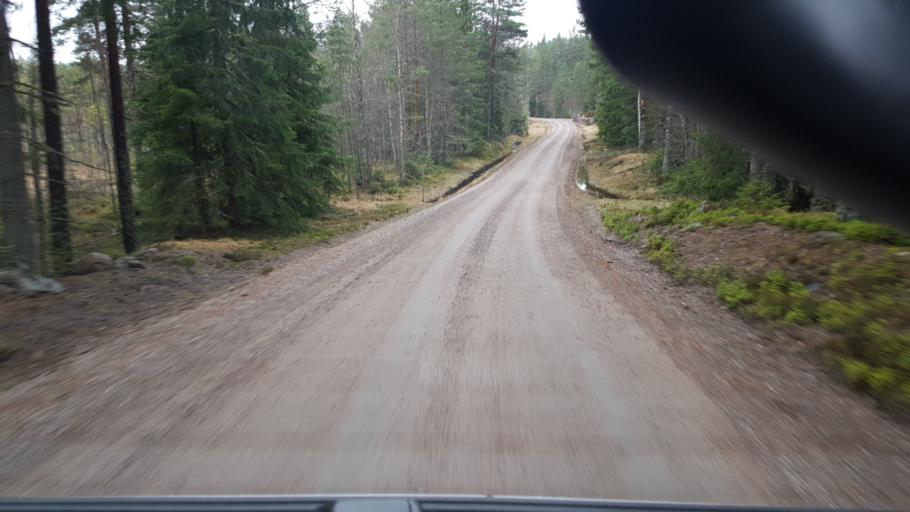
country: SE
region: Vaermland
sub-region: Eda Kommun
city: Charlottenberg
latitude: 60.0436
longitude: 12.5135
